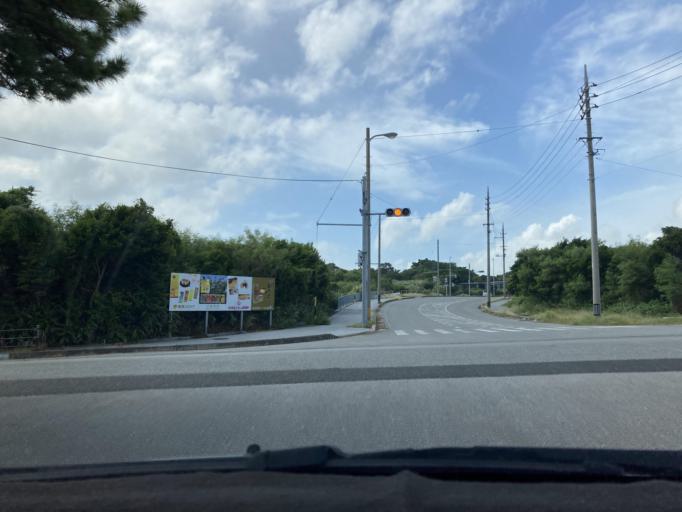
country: JP
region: Okinawa
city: Itoman
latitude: 26.0972
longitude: 127.7219
